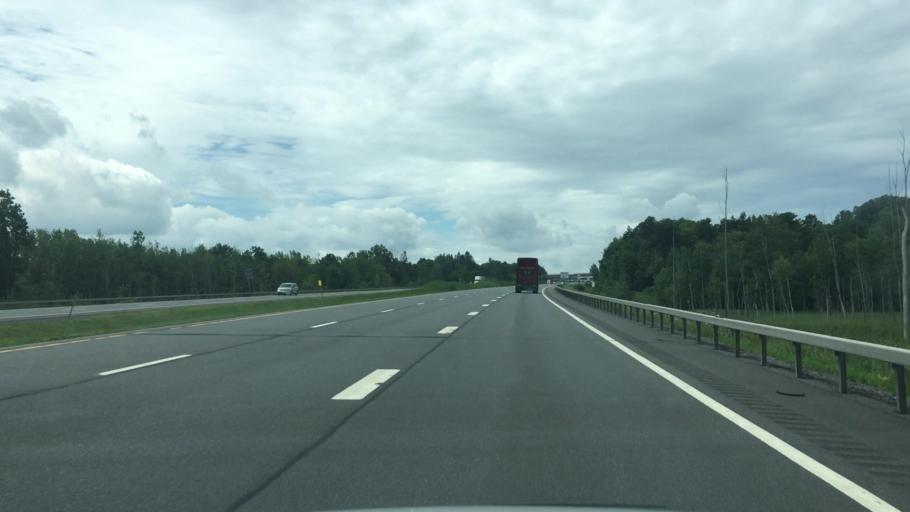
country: US
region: New York
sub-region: Albany County
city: Altamont
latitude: 42.7438
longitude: -74.1643
